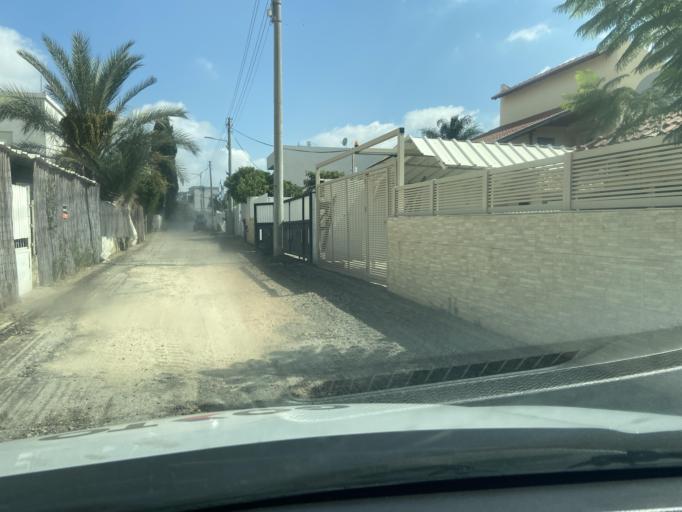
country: IL
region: Central District
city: Yehud
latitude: 32.0372
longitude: 34.8907
